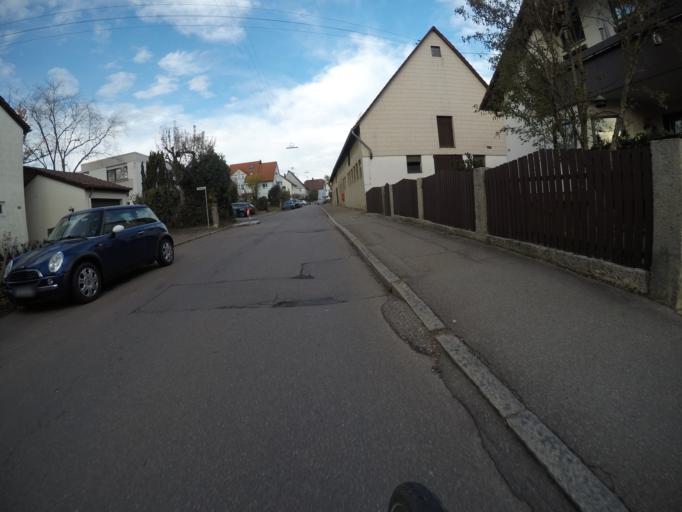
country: DE
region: Baden-Wuerttemberg
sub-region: Regierungsbezirk Stuttgart
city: Leinfelden-Echterdingen
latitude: 48.6886
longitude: 9.1639
